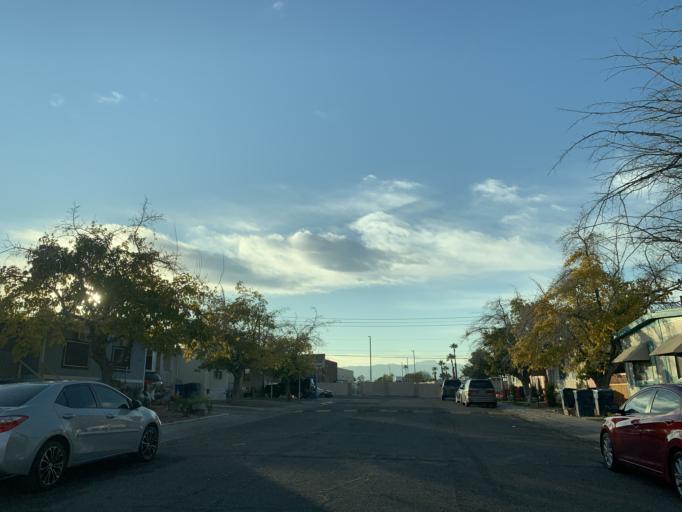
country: US
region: Nevada
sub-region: Clark County
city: Spring Valley
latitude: 36.1023
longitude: -115.2241
